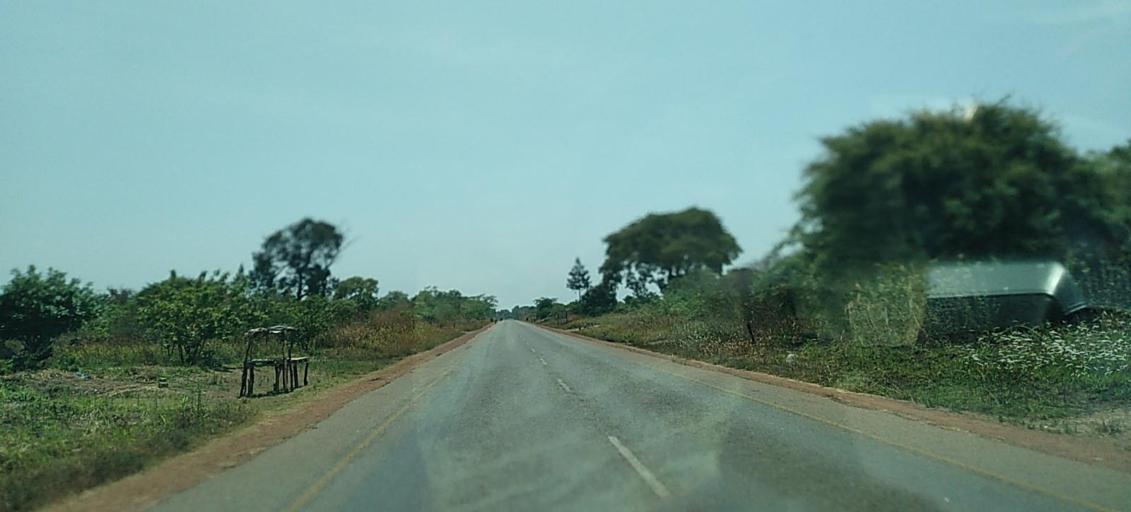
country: ZM
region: North-Western
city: Solwezi
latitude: -12.4052
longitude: 26.1388
